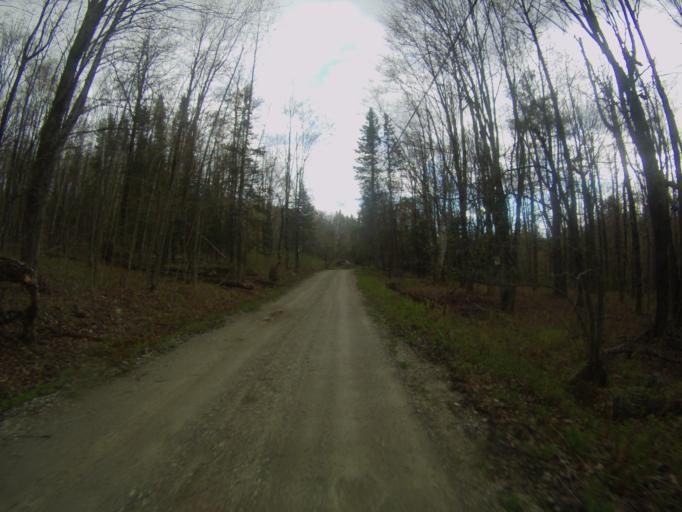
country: US
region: Vermont
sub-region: Addison County
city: Bristol
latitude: 44.0638
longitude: -73.0490
